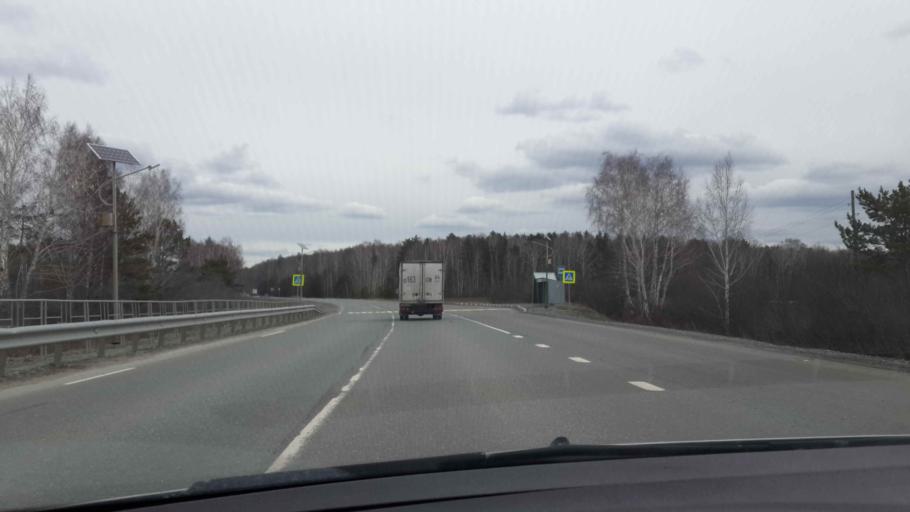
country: RU
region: Sverdlovsk
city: Verkhneye Dubrovo
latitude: 56.7404
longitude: 61.1855
